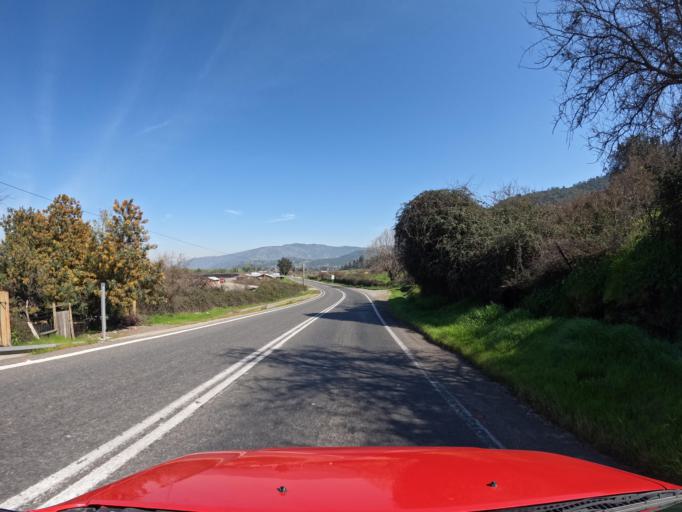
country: CL
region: Maule
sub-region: Provincia de Curico
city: Rauco
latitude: -34.9776
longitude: -71.3903
